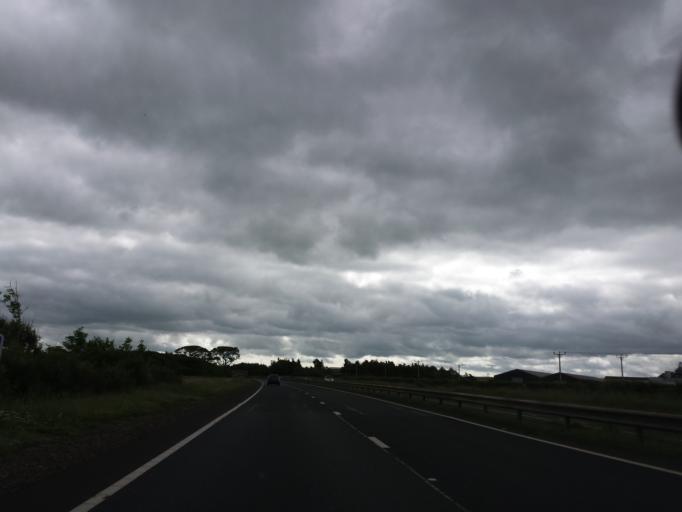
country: GB
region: Scotland
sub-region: East Lothian
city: Macmerry
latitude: 55.9490
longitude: -2.9192
